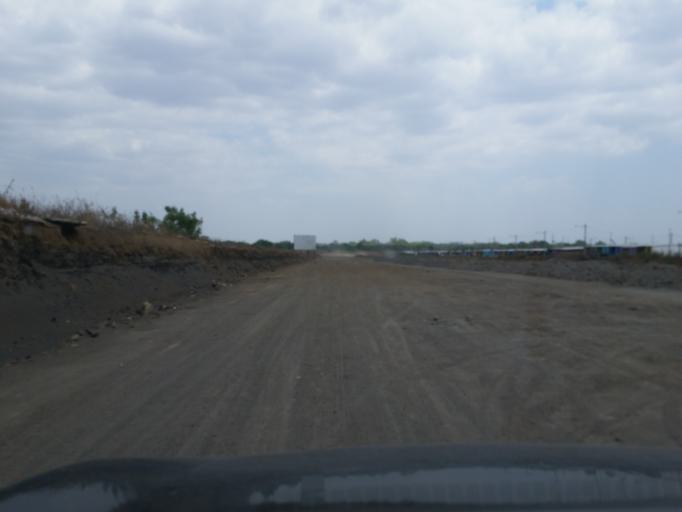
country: NI
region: Managua
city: Tipitapa
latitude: 12.1348
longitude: -86.1601
